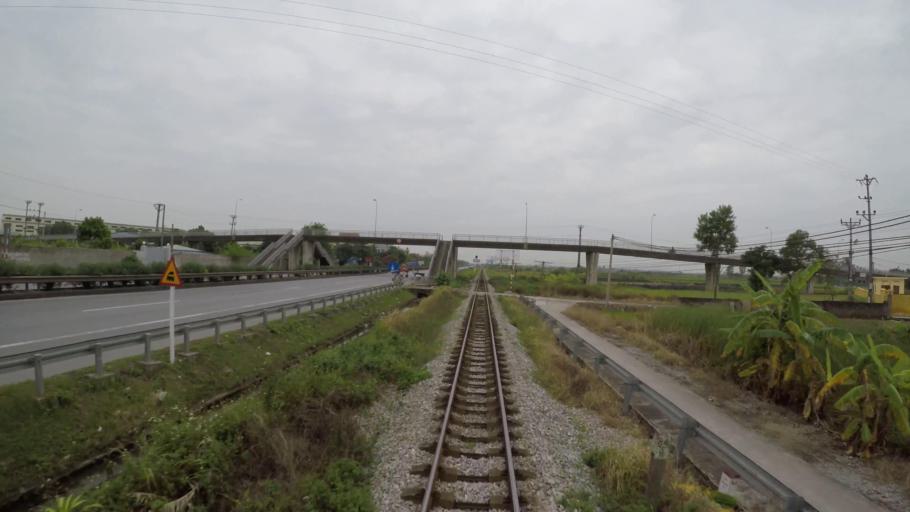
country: VN
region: Hai Duong
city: Phu Thai
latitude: 20.9405
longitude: 106.5460
